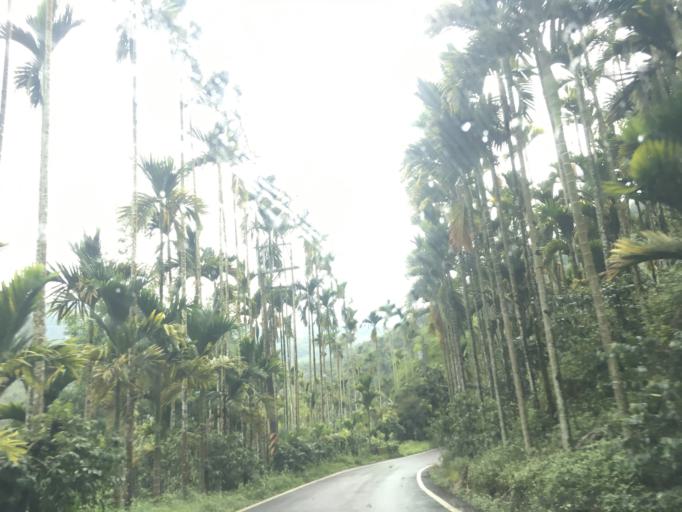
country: TW
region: Taiwan
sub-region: Yunlin
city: Douliu
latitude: 23.5693
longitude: 120.6416
